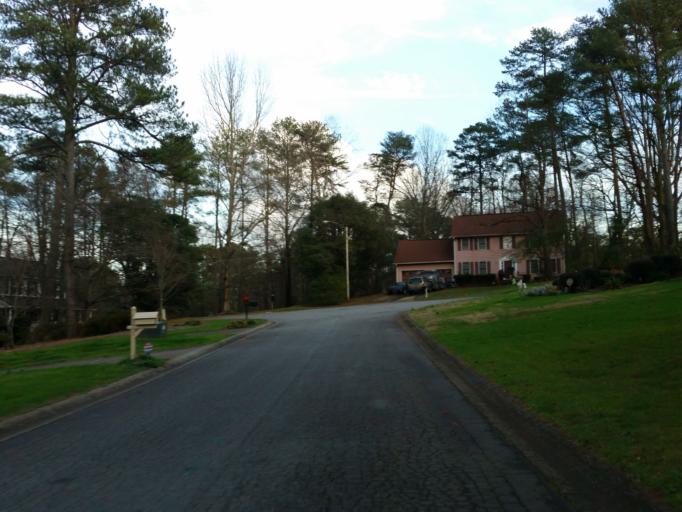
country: US
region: Georgia
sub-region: Cobb County
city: Marietta
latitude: 33.9894
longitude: -84.4916
